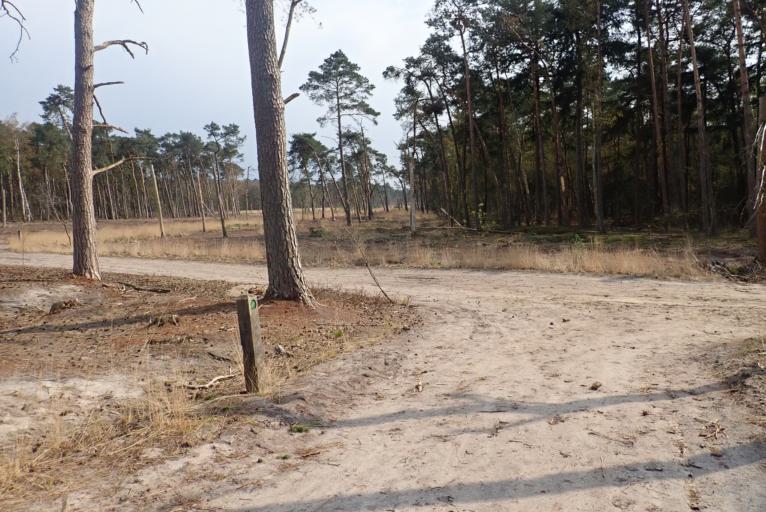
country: BE
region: Flanders
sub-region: Provincie Antwerpen
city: Kalmthout
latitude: 51.4144
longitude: 4.4503
